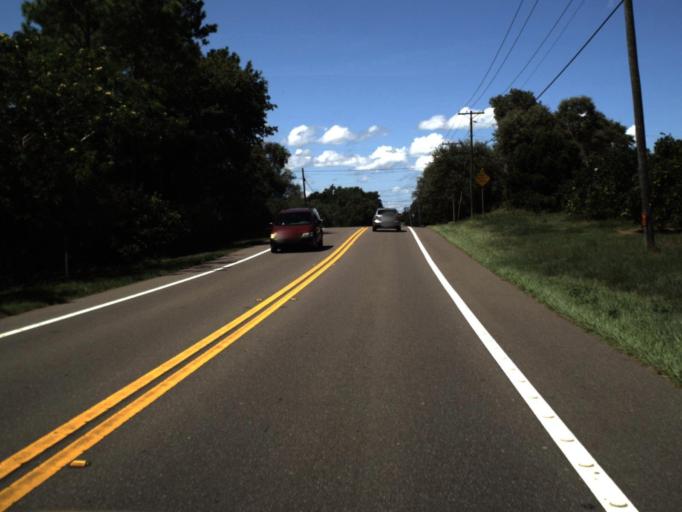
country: US
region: Florida
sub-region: Polk County
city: Crooked Lake Park
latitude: 27.8430
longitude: -81.5571
